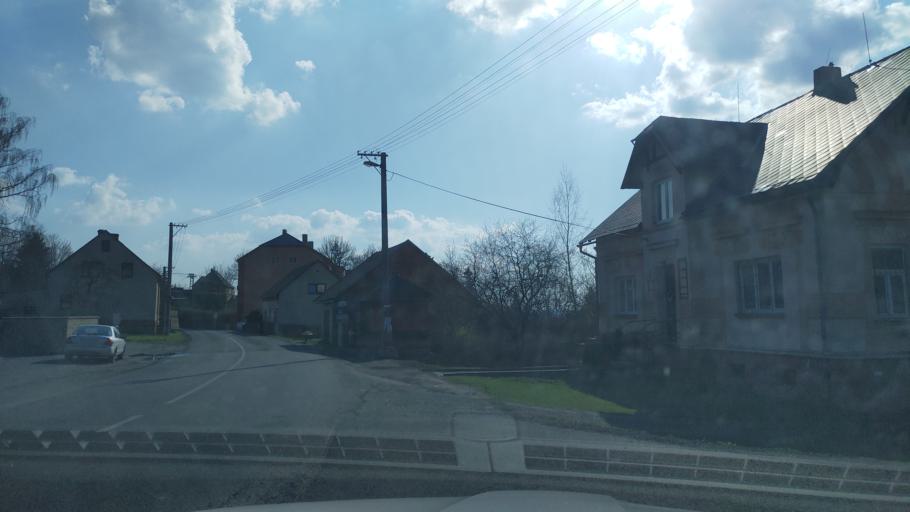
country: CZ
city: Kamenicky Senov
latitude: 50.7646
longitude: 14.4383
